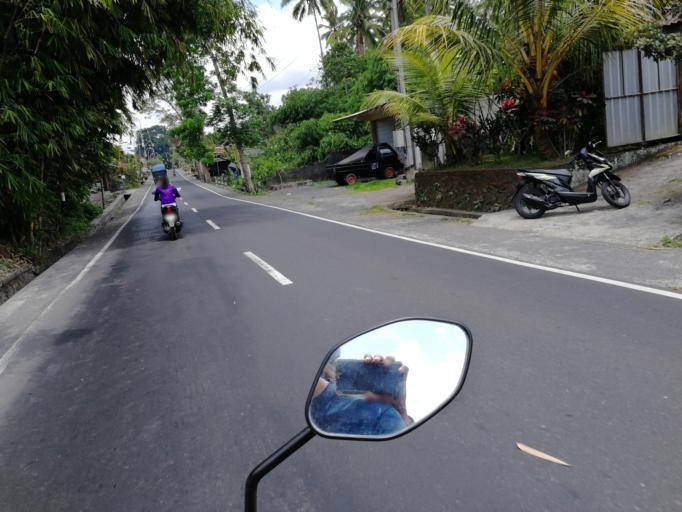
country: ID
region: Bali
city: Banjar Kubu
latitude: -8.4286
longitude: 115.4226
